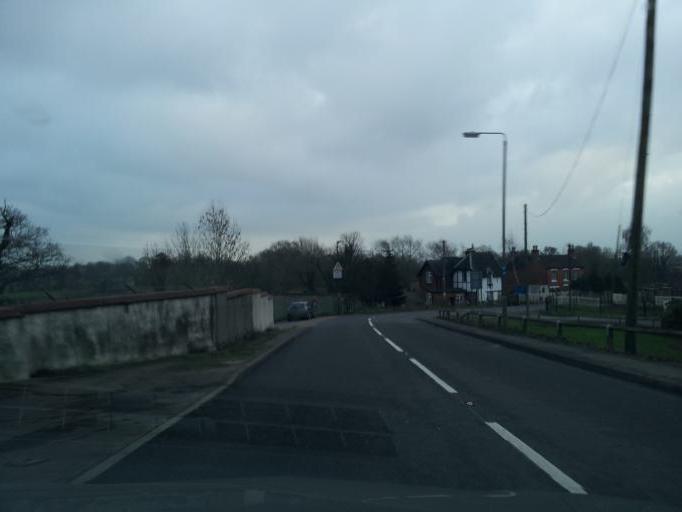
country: GB
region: England
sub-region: Derbyshire
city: Etwall
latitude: 52.8636
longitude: -1.6151
